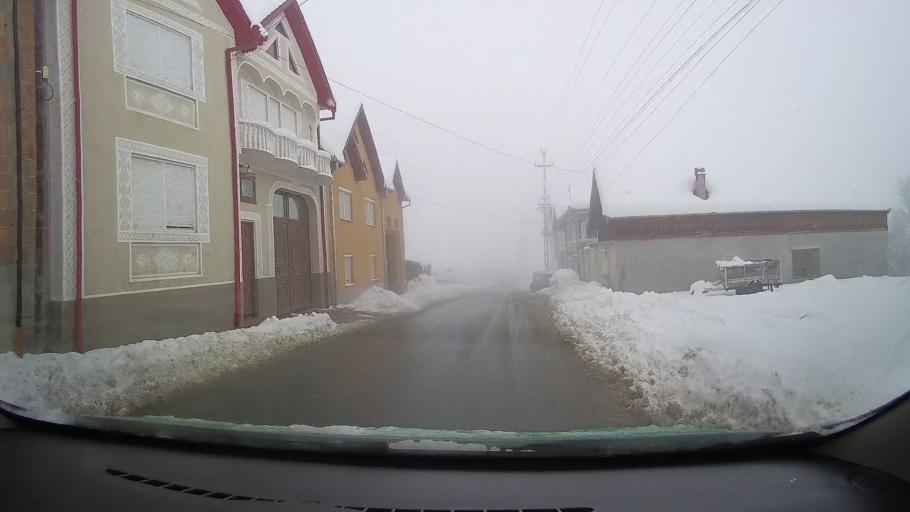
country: RO
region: Sibiu
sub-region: Comuna Jina
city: Jina
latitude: 45.7867
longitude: 23.6898
